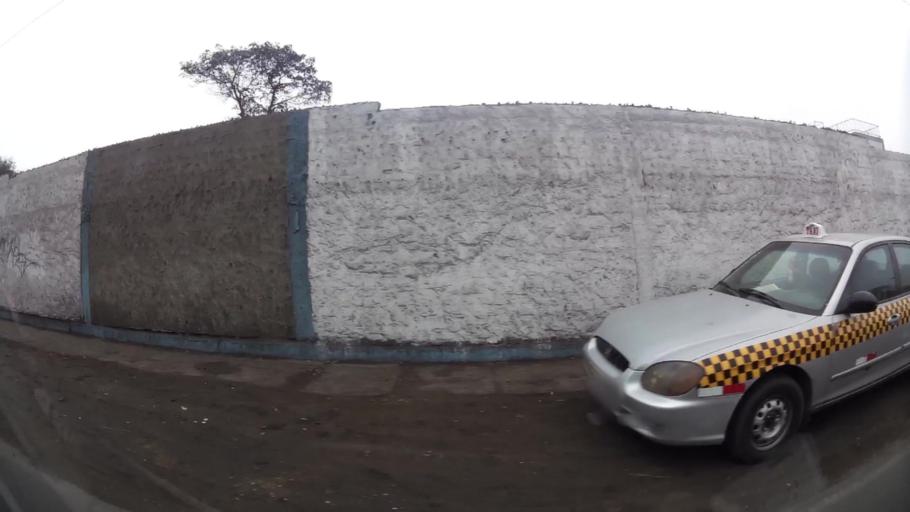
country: PE
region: Lima
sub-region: Lima
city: Surco
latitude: -12.1591
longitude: -76.9714
